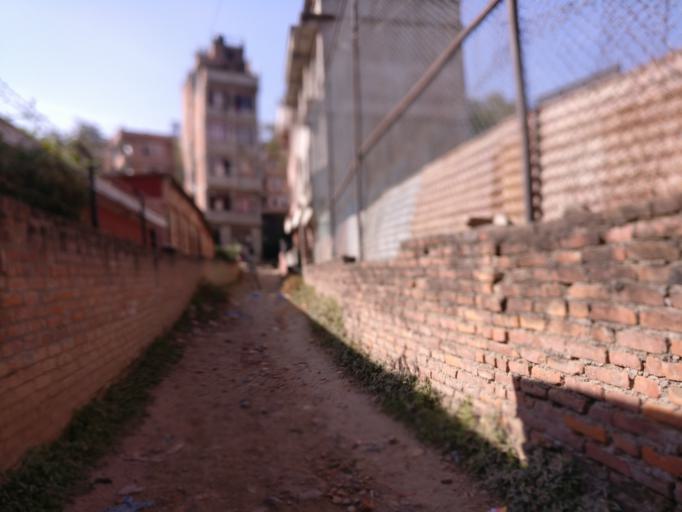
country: NP
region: Central Region
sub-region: Bagmati Zone
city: Patan
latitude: 27.6686
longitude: 85.3324
